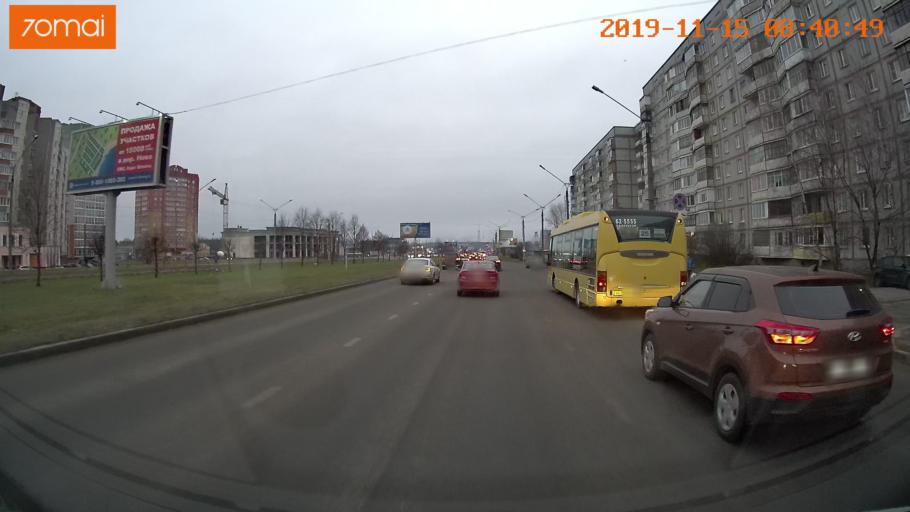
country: RU
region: Vologda
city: Cherepovets
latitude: 59.0958
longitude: 37.9132
